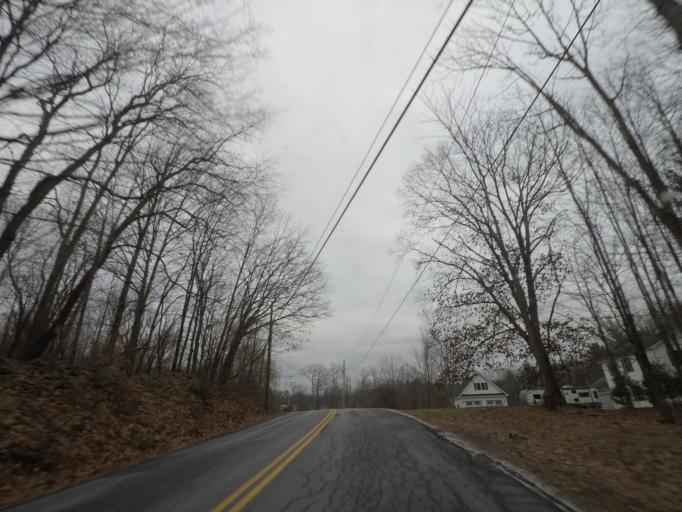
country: US
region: New York
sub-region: Rensselaer County
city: Poestenkill
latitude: 42.7623
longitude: -73.5067
